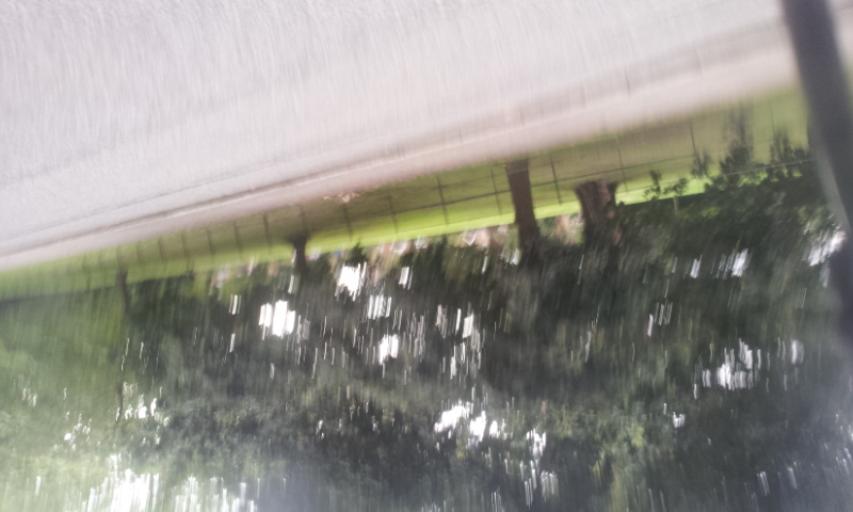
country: GB
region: England
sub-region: Kent
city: Tonbridge
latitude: 51.2038
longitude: 0.2813
